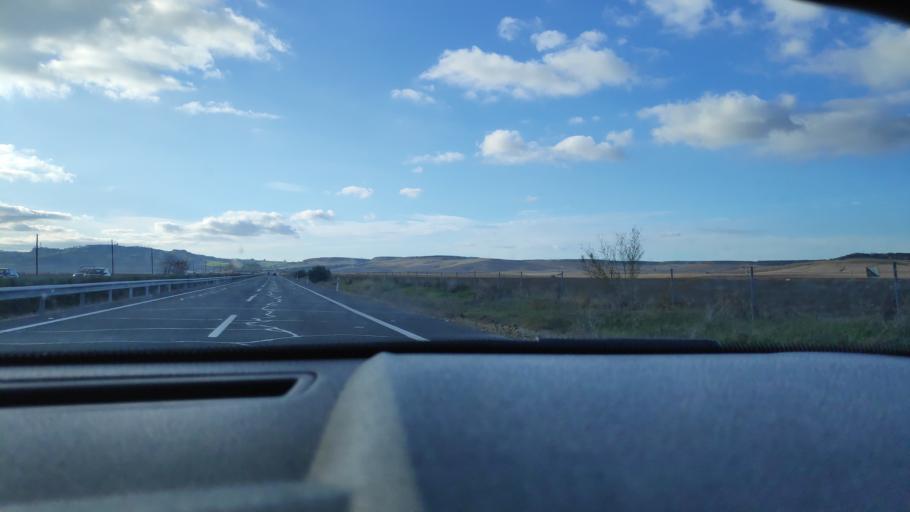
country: ES
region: Andalusia
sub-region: Provincia de Sevilla
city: Carmona
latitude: 37.4797
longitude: -5.5803
